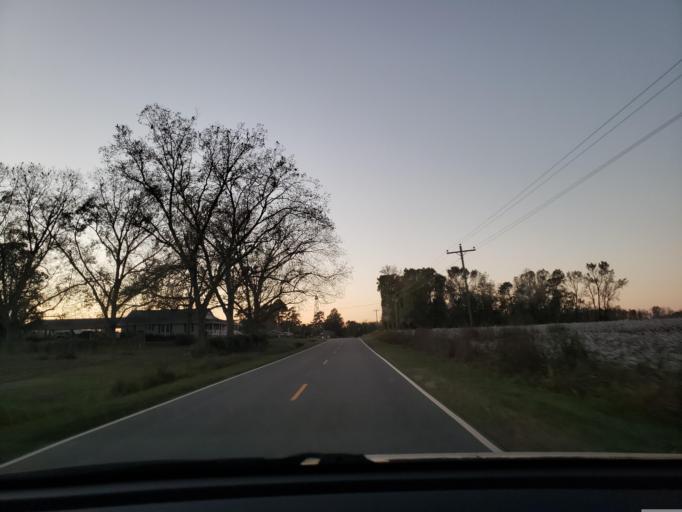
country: US
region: North Carolina
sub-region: Duplin County
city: Beulaville
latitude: 34.7895
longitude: -77.7610
